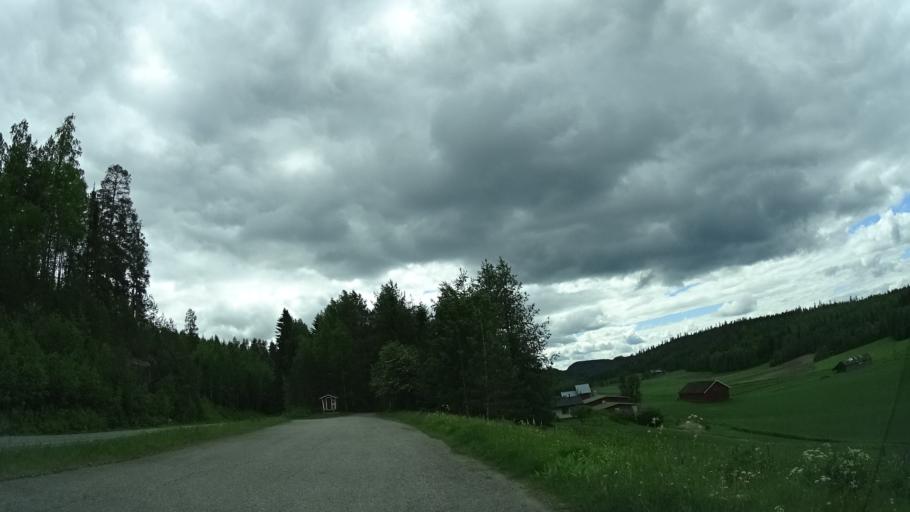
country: FI
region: Central Finland
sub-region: Jyvaeskylae
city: Toivakka
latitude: 62.0568
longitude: 26.0284
